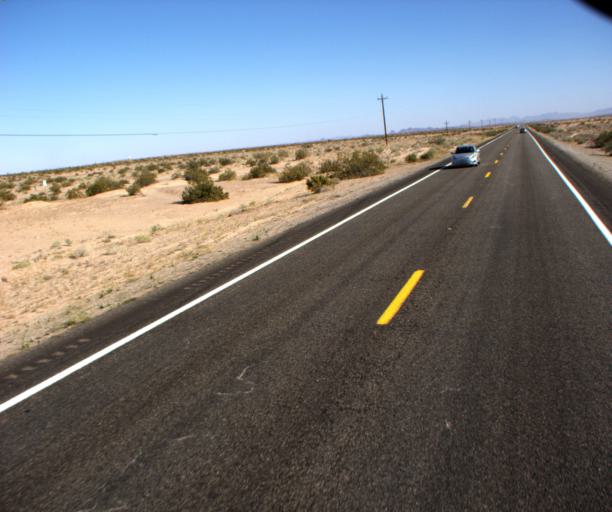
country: US
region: Arizona
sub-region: Yuma County
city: Fortuna Foothills
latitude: 32.8334
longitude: -114.3722
